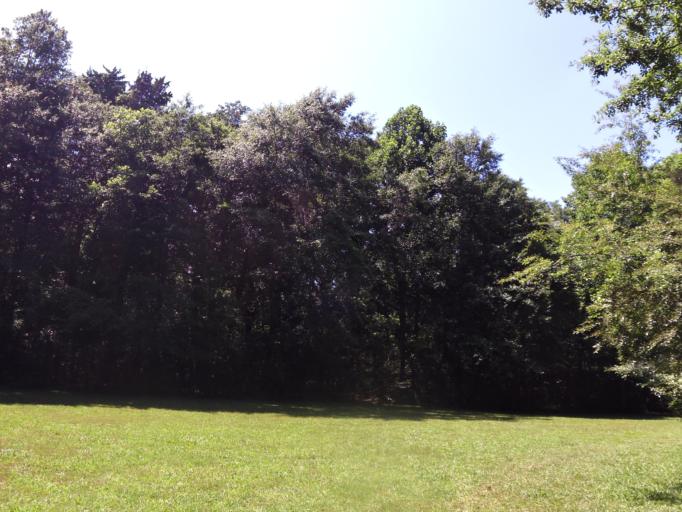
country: US
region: Mississippi
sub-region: Lafayette County
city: University
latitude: 34.3600
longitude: -89.5256
